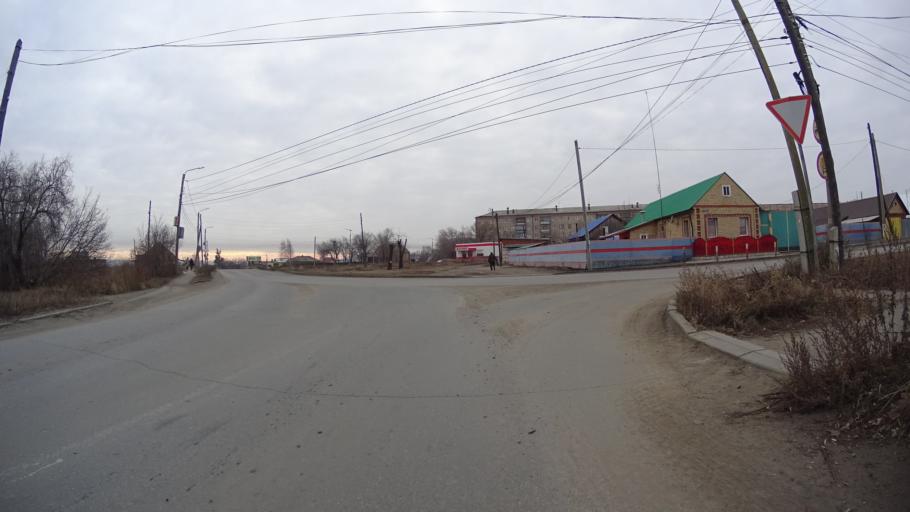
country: RU
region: Chelyabinsk
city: Troitsk
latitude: 54.1046
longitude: 61.5629
